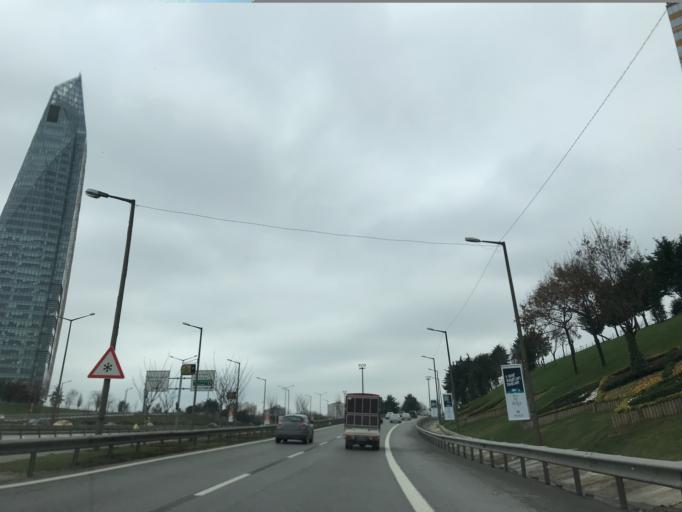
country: TR
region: Istanbul
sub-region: Atasehir
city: Atasehir
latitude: 40.9841
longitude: 29.1026
